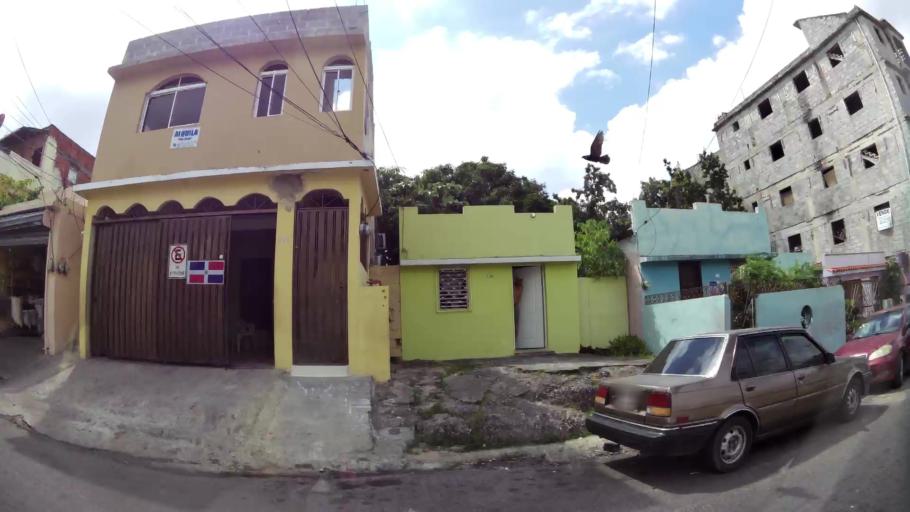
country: DO
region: Nacional
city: La Agustina
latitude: 18.4913
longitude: -69.9332
